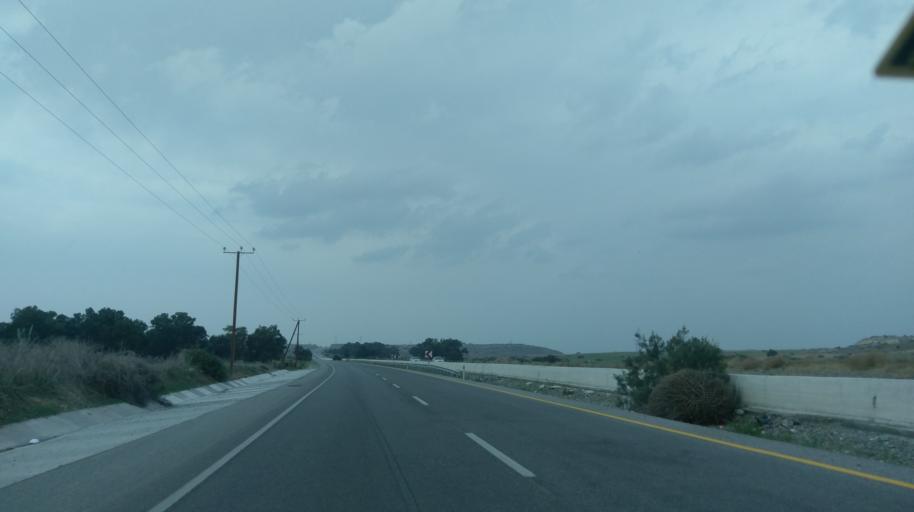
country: CY
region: Lefkosia
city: Peristerona
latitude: 35.1958
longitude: 33.0956
